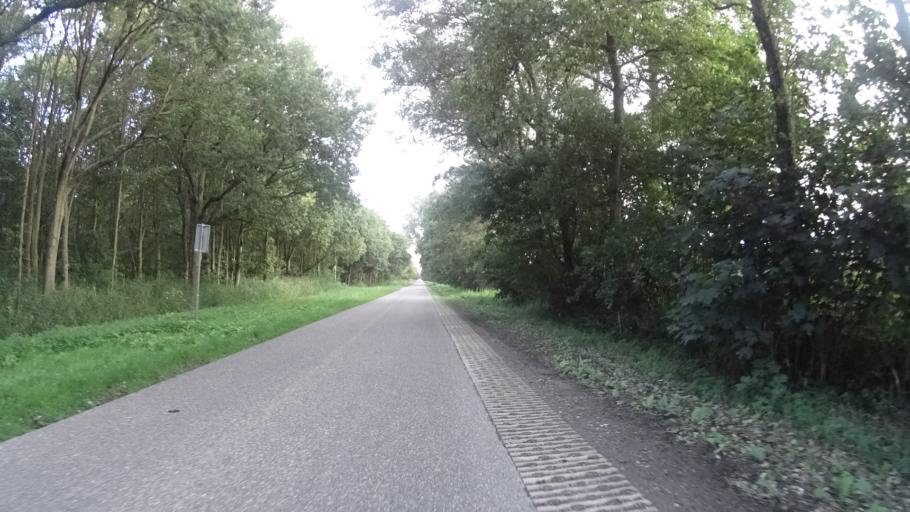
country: NL
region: North Holland
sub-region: Gemeente Hollands Kroon
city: Den Oever
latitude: 52.9079
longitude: 5.0607
